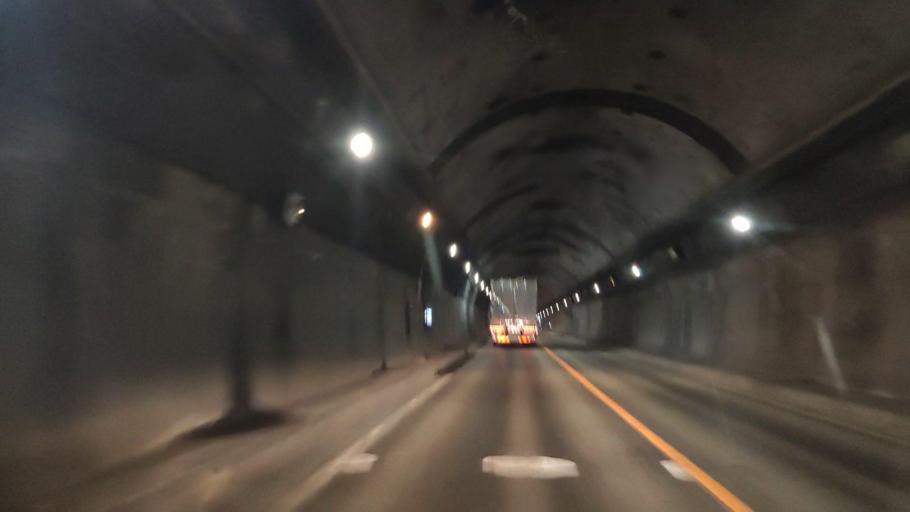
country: JP
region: Aomori
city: Aomori Shi
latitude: 40.7762
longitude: 140.9677
